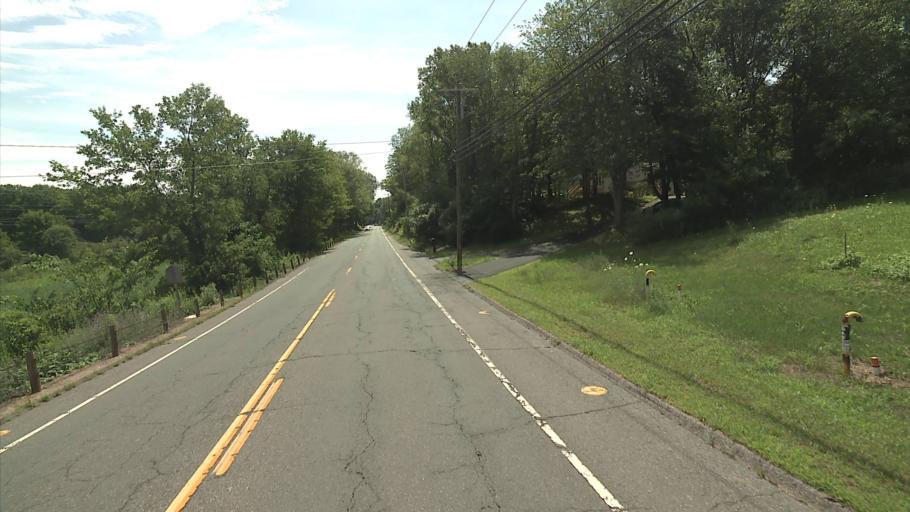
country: US
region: Connecticut
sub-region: Tolland County
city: South Coventry
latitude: 41.7641
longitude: -72.2870
